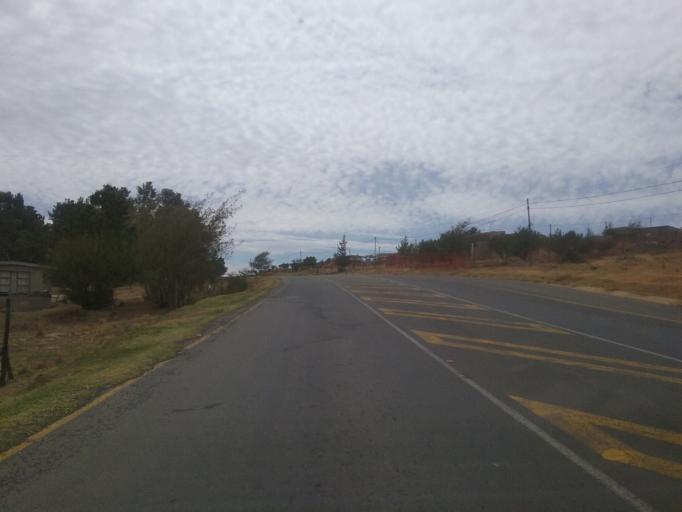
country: LS
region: Maseru
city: Nako
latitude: -29.6297
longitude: 27.4845
